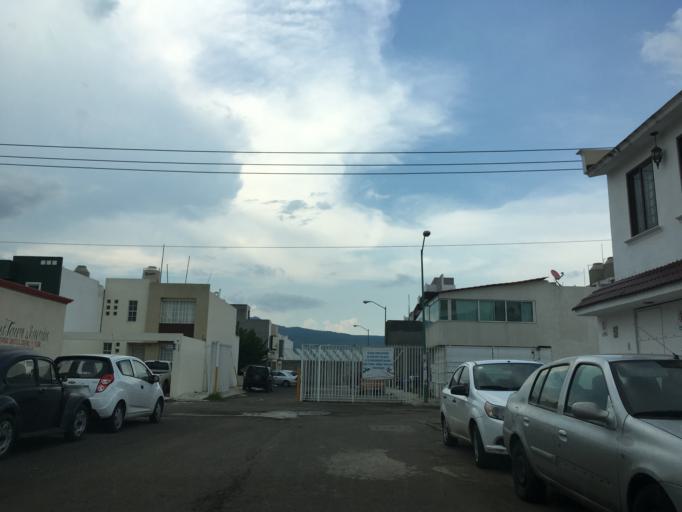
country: MX
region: Michoacan
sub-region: Morelia
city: Morelos
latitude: 19.6713
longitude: -101.2409
